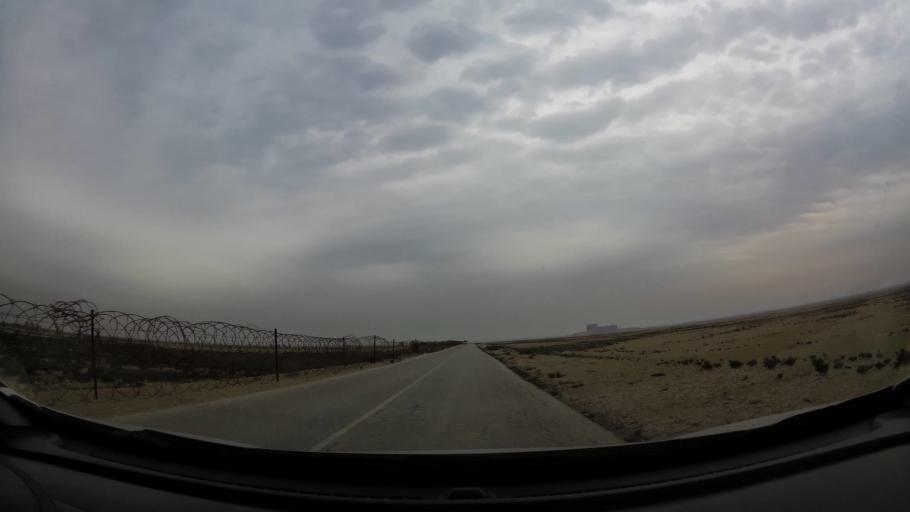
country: BH
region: Central Governorate
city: Dar Kulayb
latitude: 25.8800
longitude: 50.5890
